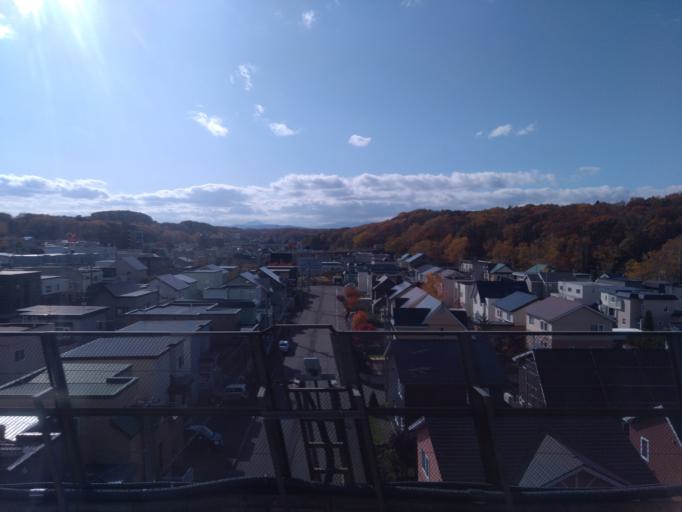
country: JP
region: Hokkaido
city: Kitahiroshima
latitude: 42.9869
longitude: 141.5610
